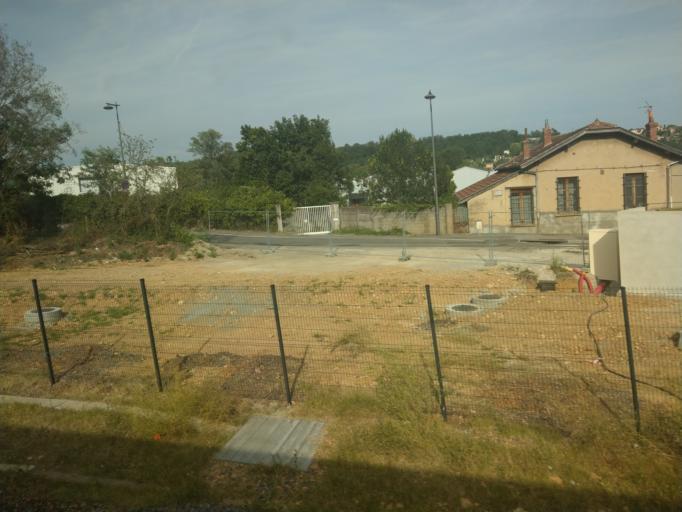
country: FR
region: Rhone-Alpes
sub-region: Departement du Rhone
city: Albigny-sur-Saone
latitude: 45.8513
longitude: 4.8303
